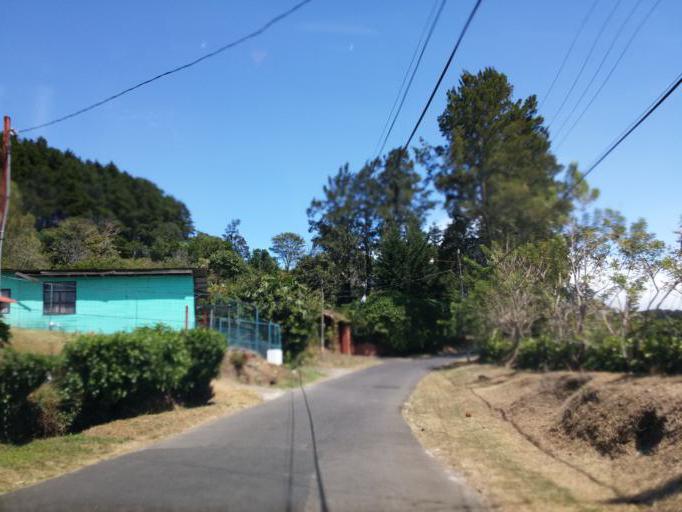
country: CR
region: Heredia
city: Santo Domingo
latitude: 10.0640
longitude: -84.1305
